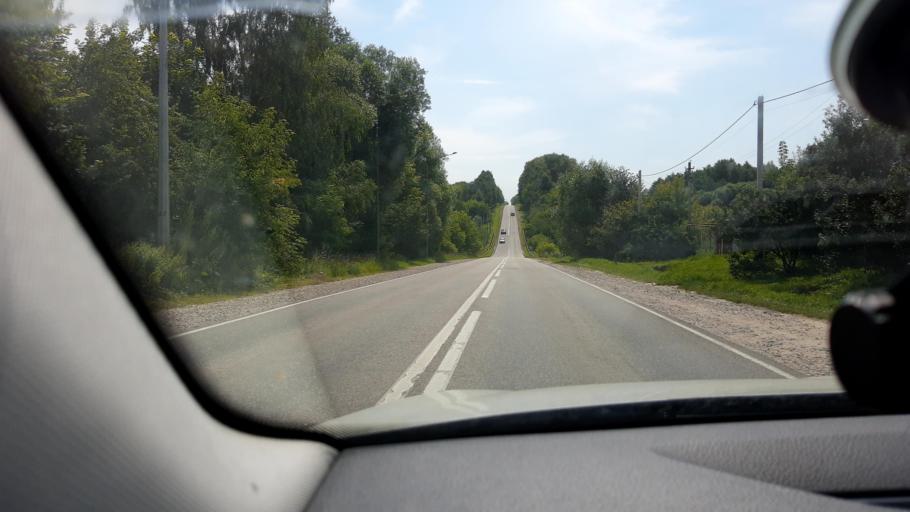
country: RU
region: Tula
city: Zaokskiy
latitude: 54.7942
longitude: 37.4327
